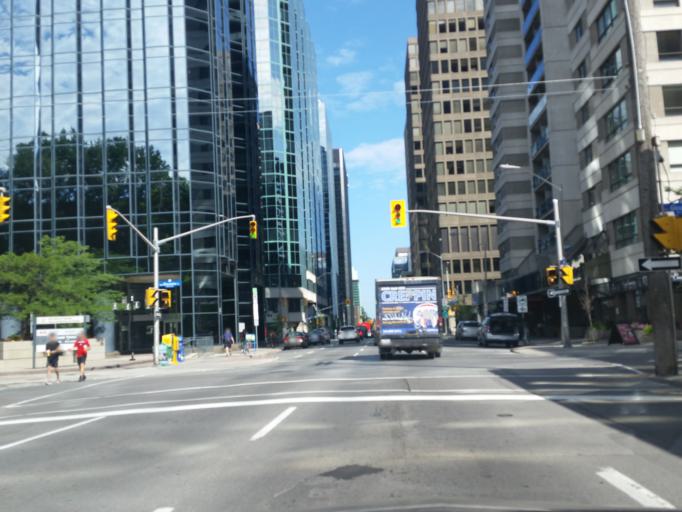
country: CA
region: Ontario
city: Ottawa
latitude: 45.4169
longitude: -75.7005
